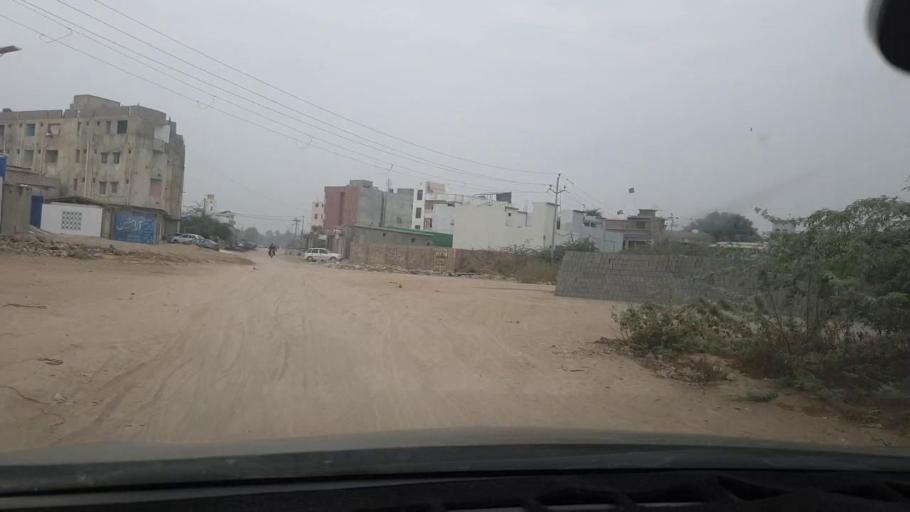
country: PK
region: Sindh
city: Malir Cantonment
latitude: 24.9212
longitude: 67.2608
